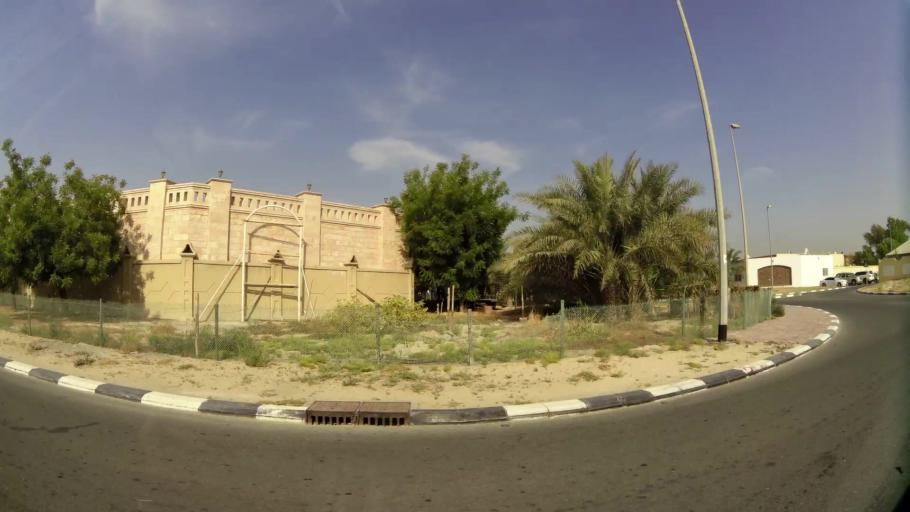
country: AE
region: Ash Shariqah
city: Sharjah
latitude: 25.2444
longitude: 55.4142
